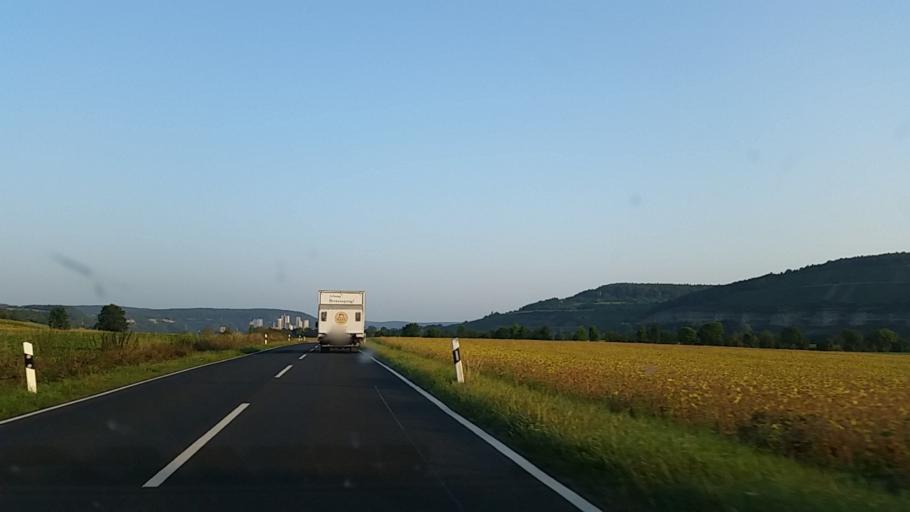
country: DE
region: Bavaria
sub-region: Regierungsbezirk Unterfranken
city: Himmelstadt
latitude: 49.9328
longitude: 9.7954
